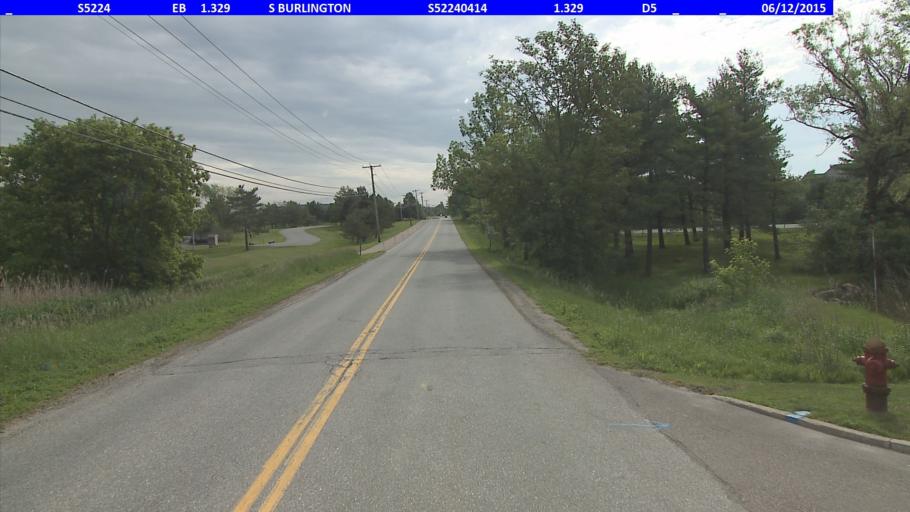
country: US
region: Vermont
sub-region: Chittenden County
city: South Burlington
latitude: 44.4425
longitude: -73.1835
